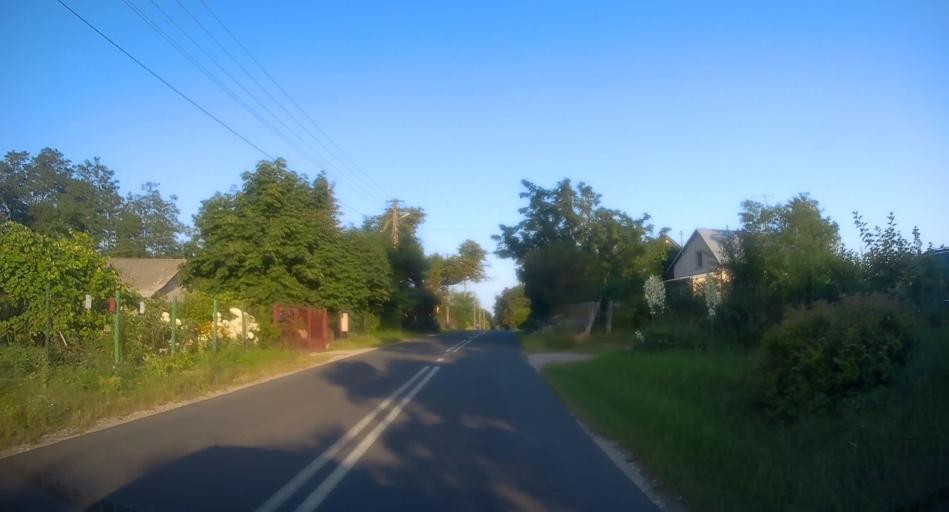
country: PL
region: Lodz Voivodeship
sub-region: Powiat skierniewicki
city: Kowiesy
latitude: 51.9006
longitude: 20.3697
